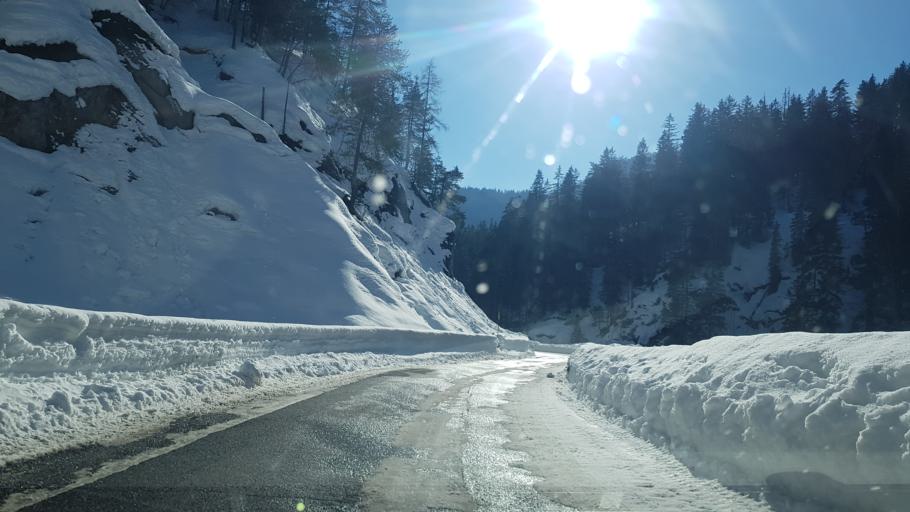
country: IT
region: Friuli Venezia Giulia
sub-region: Provincia di Udine
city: Malborghetto
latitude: 46.5342
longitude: 13.4718
